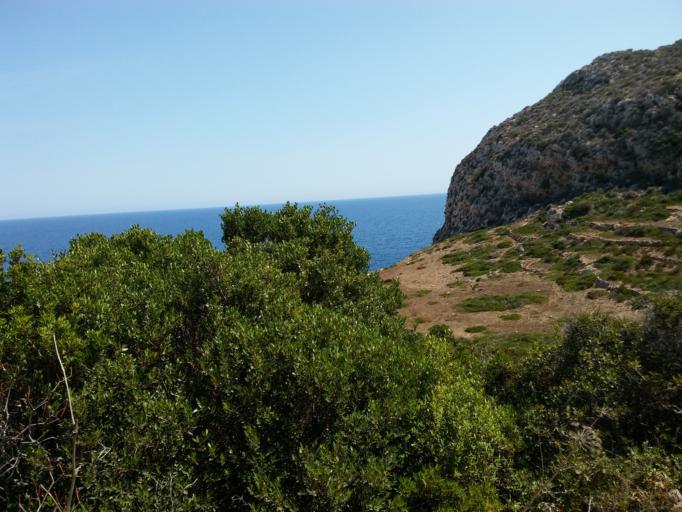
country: IT
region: Sicily
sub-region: Trapani
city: Favignana
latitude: 37.9977
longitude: 12.3456
